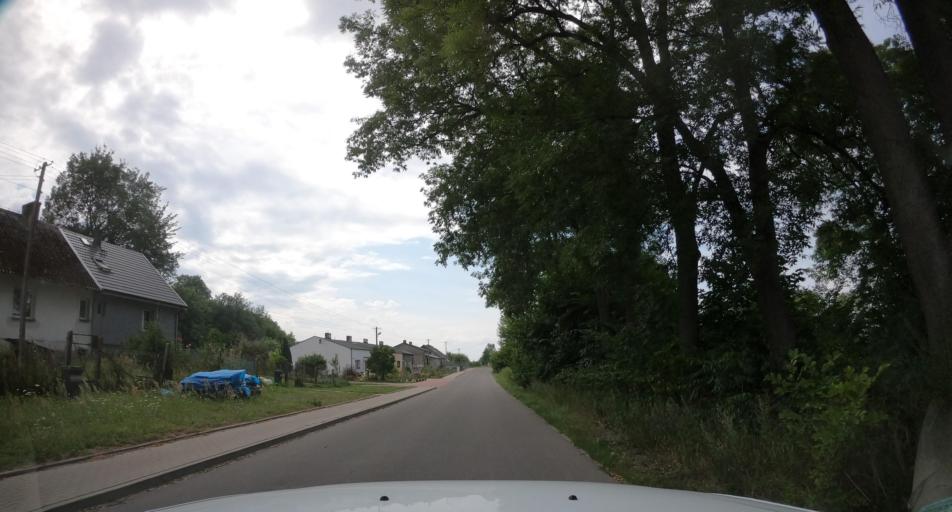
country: PL
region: West Pomeranian Voivodeship
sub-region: Powiat walecki
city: Tuczno
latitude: 53.2315
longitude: 16.2426
